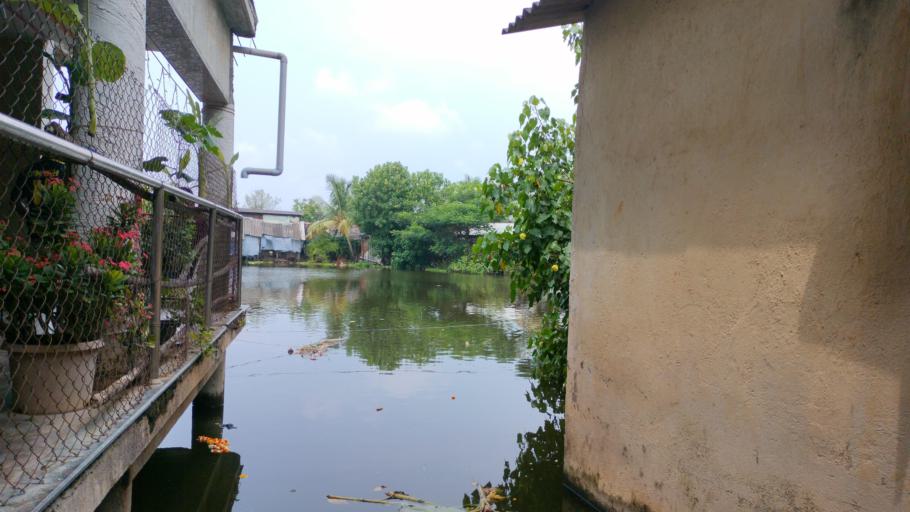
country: IN
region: Maharashtra
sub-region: Thane
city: Virar
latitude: 19.3877
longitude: 72.7748
